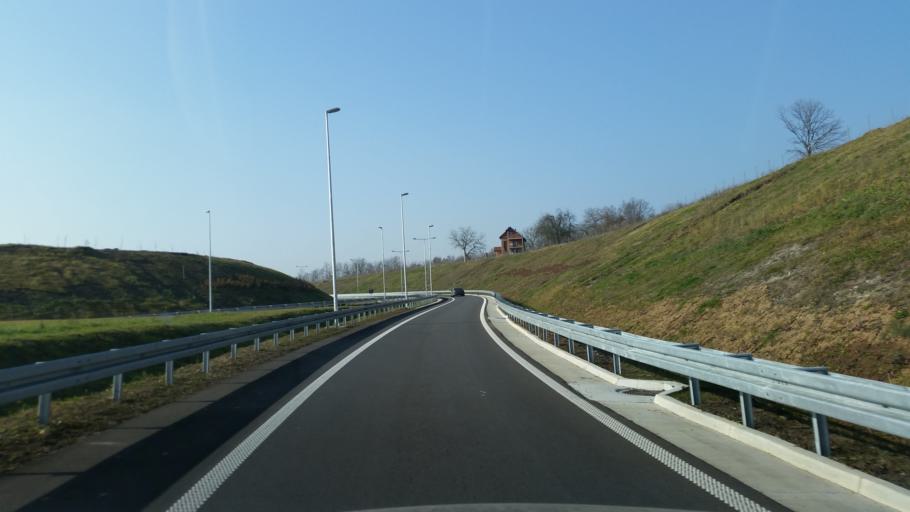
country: RS
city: Prislonica
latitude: 43.9230
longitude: 20.3974
